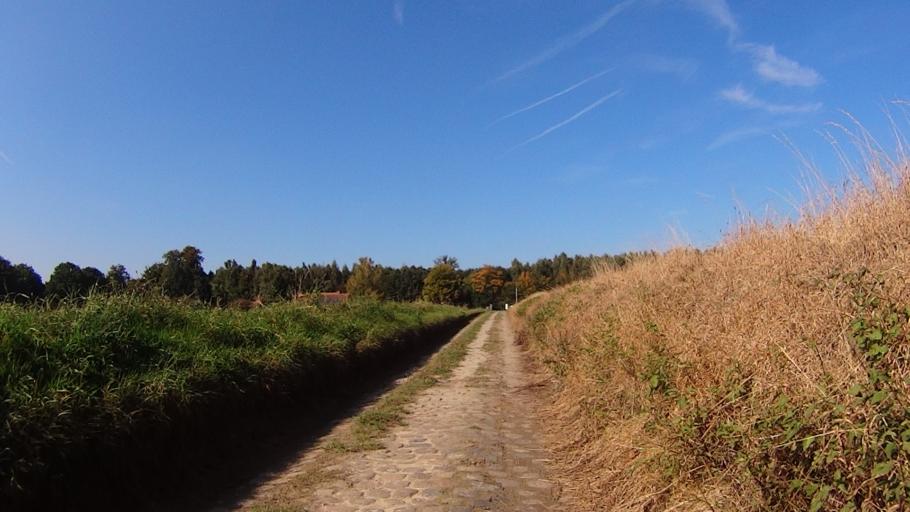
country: BE
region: Flanders
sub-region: Provincie Vlaams-Brabant
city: Hoeilaart
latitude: 50.7888
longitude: 4.4736
